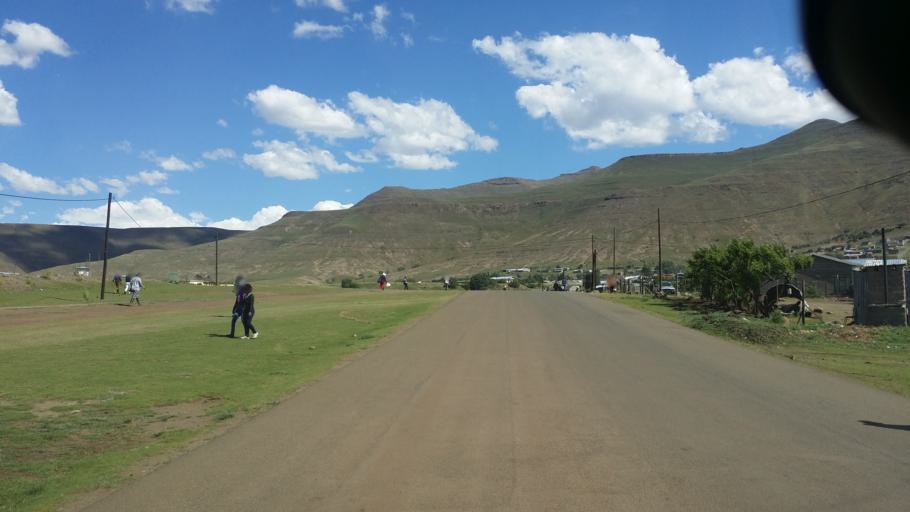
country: LS
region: Mokhotlong
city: Mokhotlong
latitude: -29.2811
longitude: 29.0678
